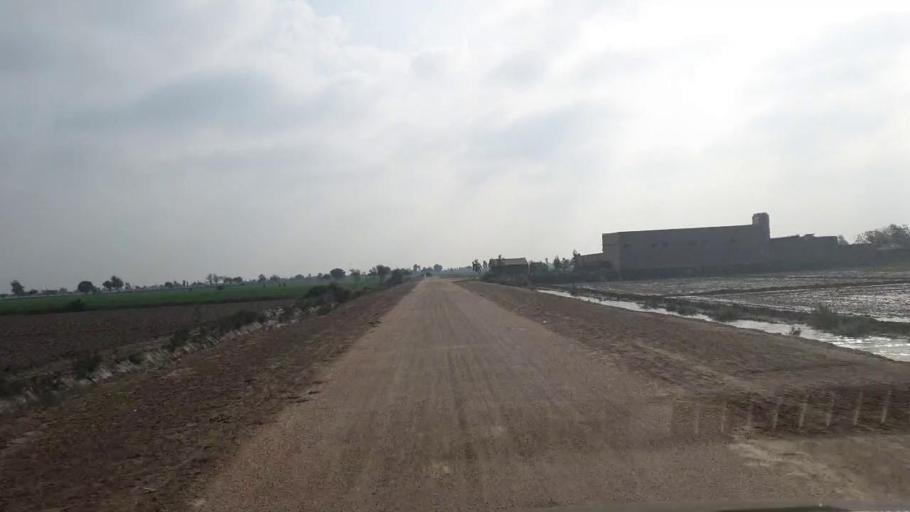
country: PK
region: Sindh
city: Shahdadpur
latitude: 25.9009
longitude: 68.6577
